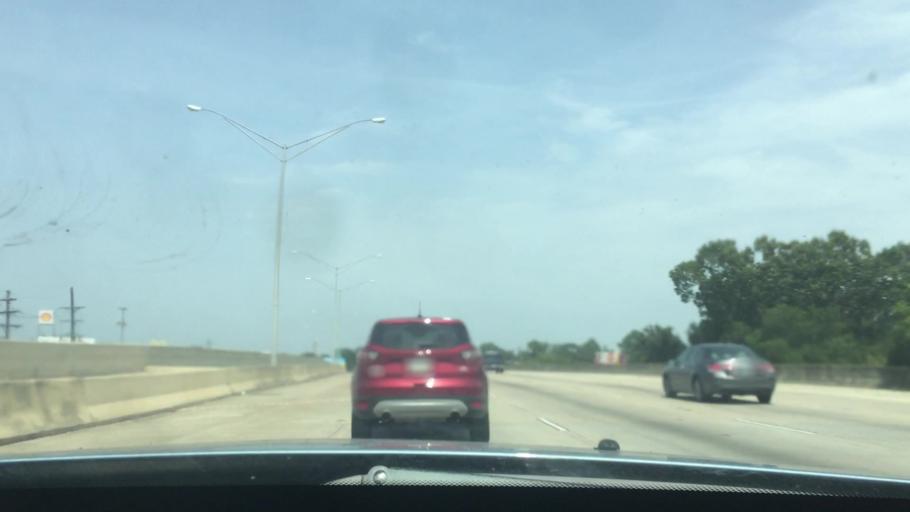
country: US
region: Louisiana
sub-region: East Baton Rouge Parish
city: Westminster
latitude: 30.4171
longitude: -91.0922
